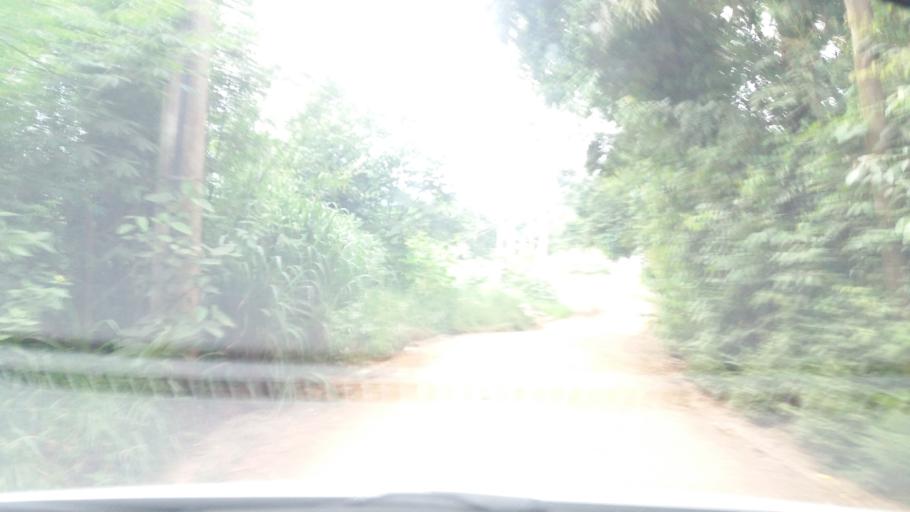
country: BR
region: Sao Paulo
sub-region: Bom Jesus Dos Perdoes
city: Bom Jesus dos Perdoes
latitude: -23.1461
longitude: -46.4620
